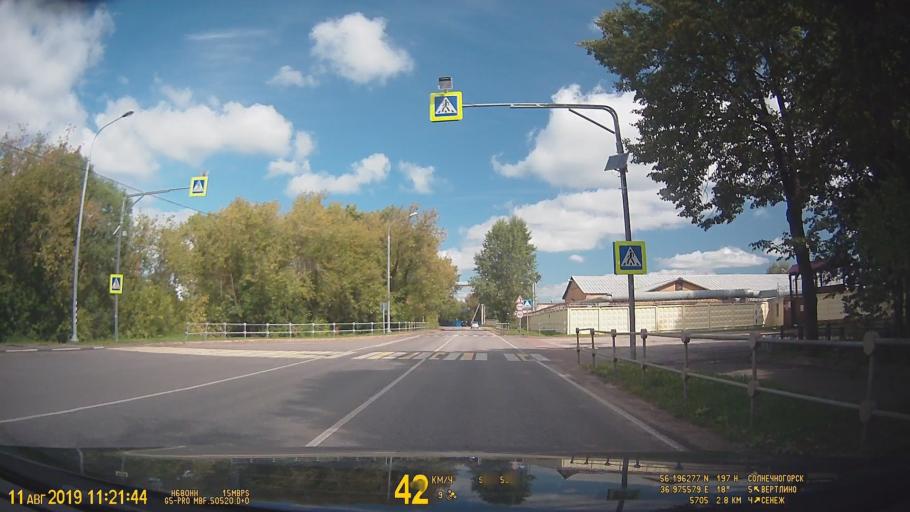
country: RU
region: Moskovskaya
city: Solnechnogorsk
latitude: 56.1964
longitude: 36.9757
